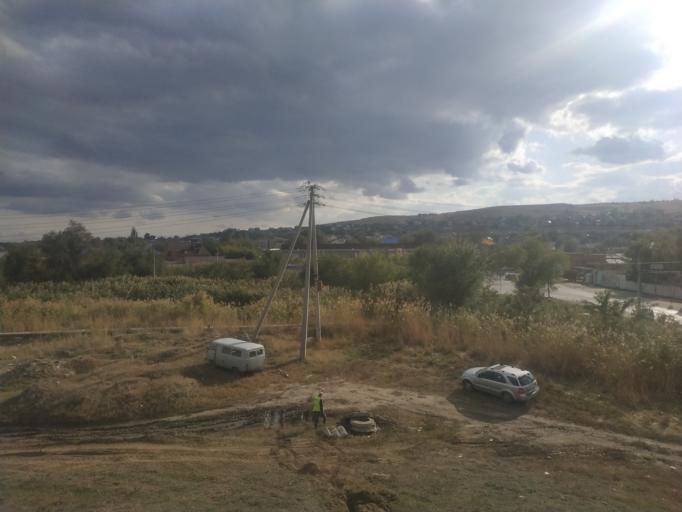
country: RU
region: Volgograd
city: Krasnoslobodsk
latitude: 48.5066
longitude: 44.5481
